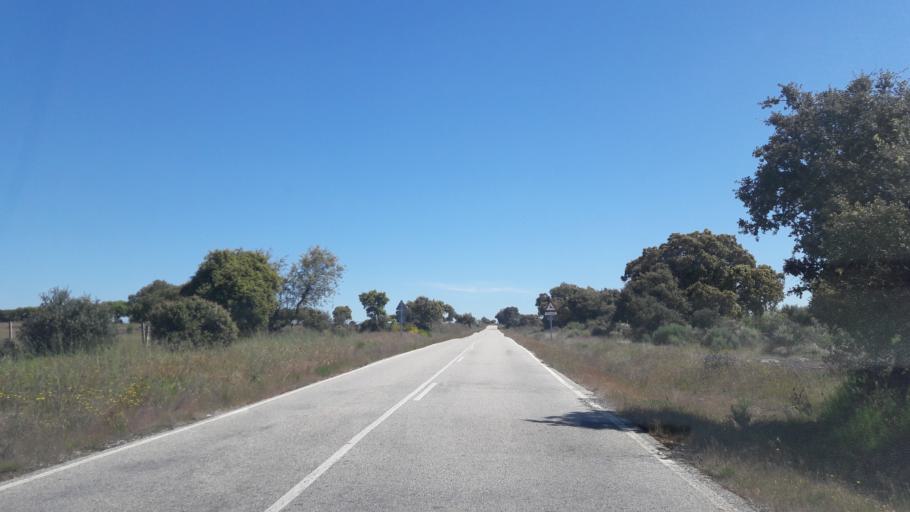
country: ES
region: Castille and Leon
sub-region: Provincia de Salamanca
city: Villarmuerto
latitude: 41.0382
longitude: -6.3933
